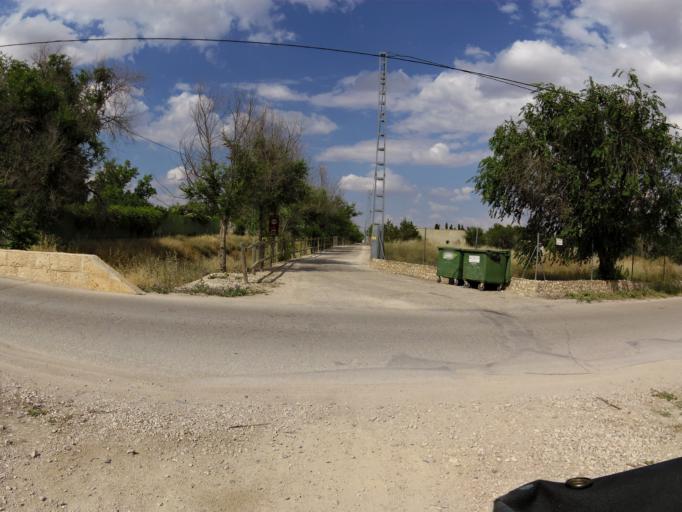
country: ES
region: Castille-La Mancha
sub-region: Provincia de Albacete
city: Albacete
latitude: 38.9734
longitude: -1.9290
